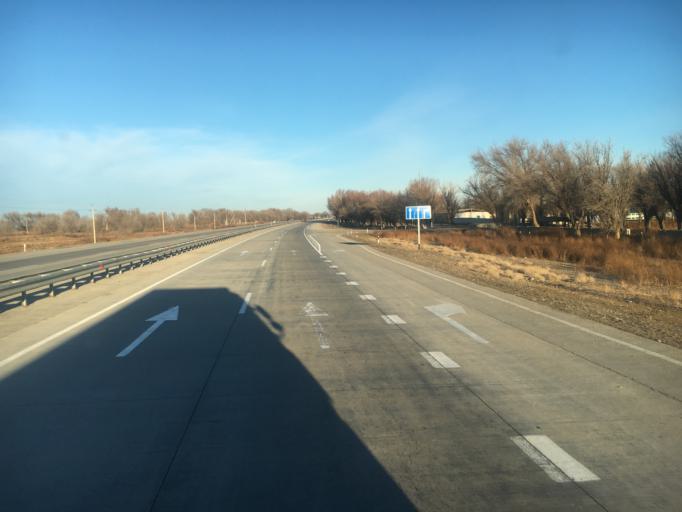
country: KZ
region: Ongtustik Qazaqstan
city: Turkestan
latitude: 43.1445
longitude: 68.5784
